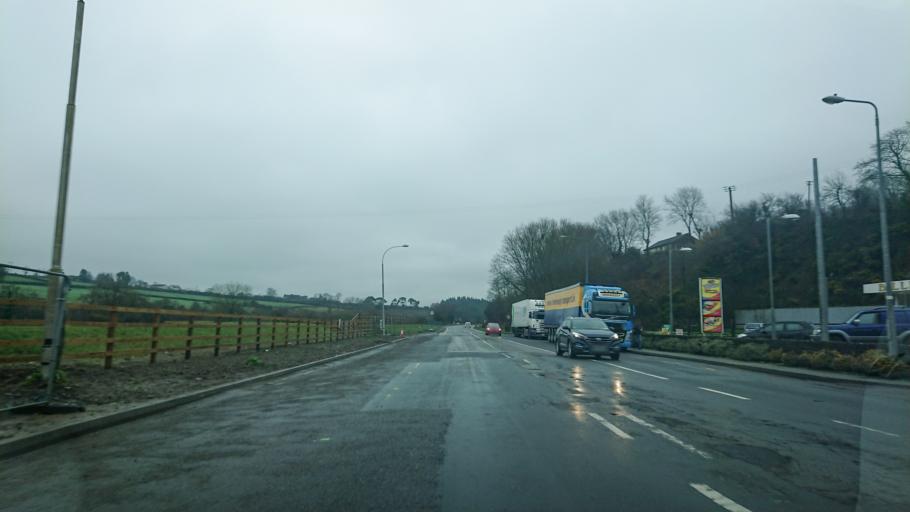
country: IE
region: Munster
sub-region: County Cork
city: Bandon
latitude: 51.7528
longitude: -8.7170
